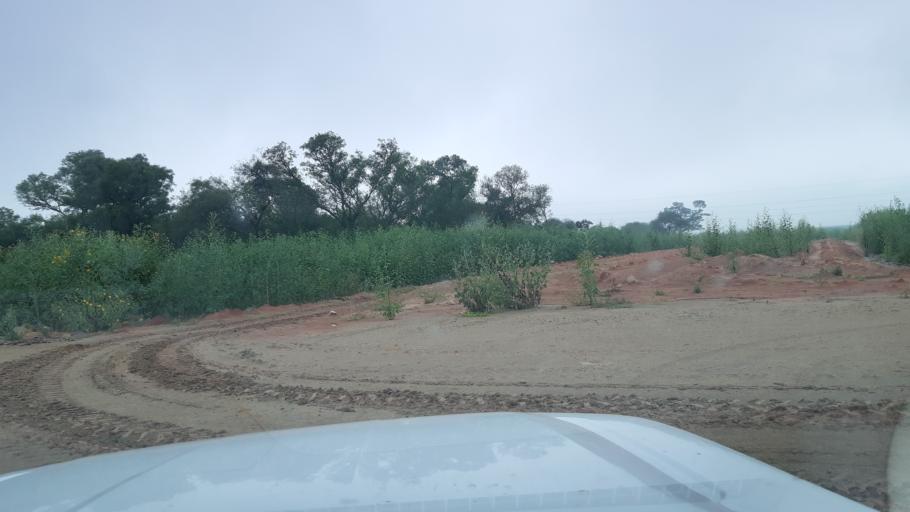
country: AR
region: Jujuy
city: La Mendieta
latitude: -24.3743
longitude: -65.0032
